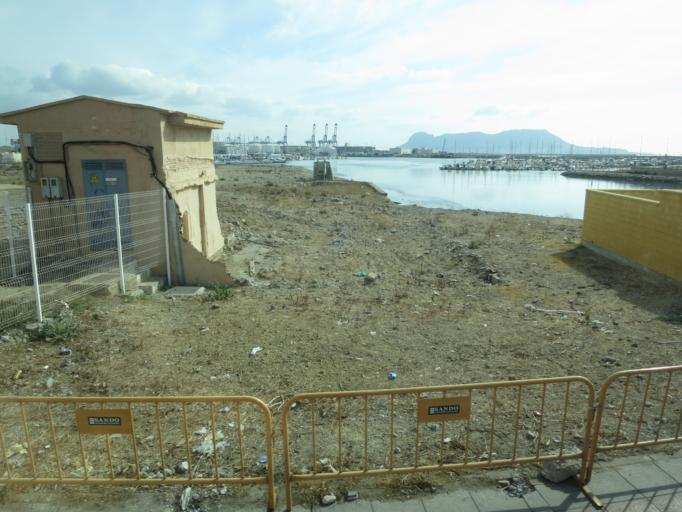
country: ES
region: Andalusia
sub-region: Provincia de Cadiz
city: Algeciras
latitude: 36.1184
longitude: -5.4432
